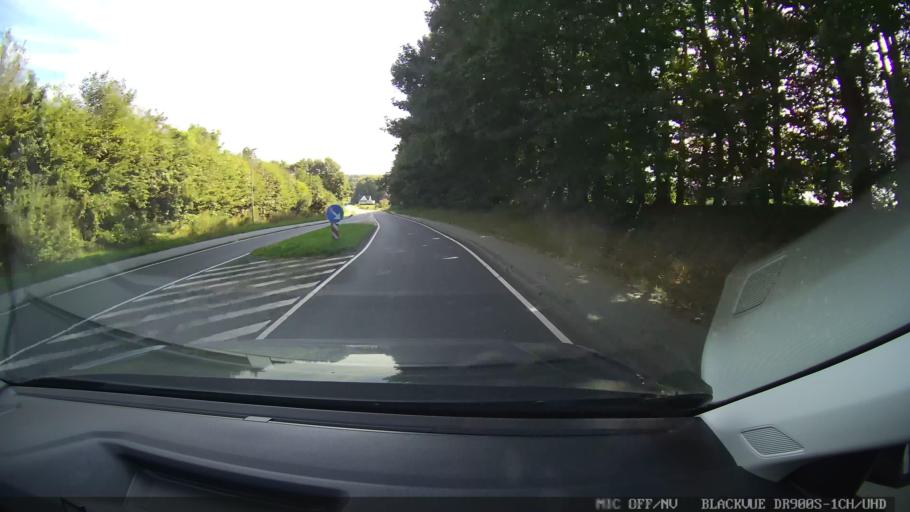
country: DK
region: North Denmark
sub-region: Mariagerfjord Kommune
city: Arden
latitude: 56.7822
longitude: 9.7151
